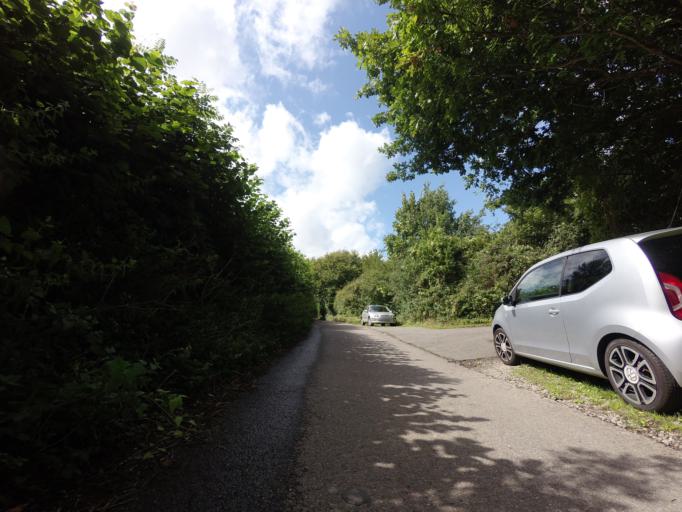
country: GB
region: England
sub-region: Kent
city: Borough Green
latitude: 51.2623
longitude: 0.3022
